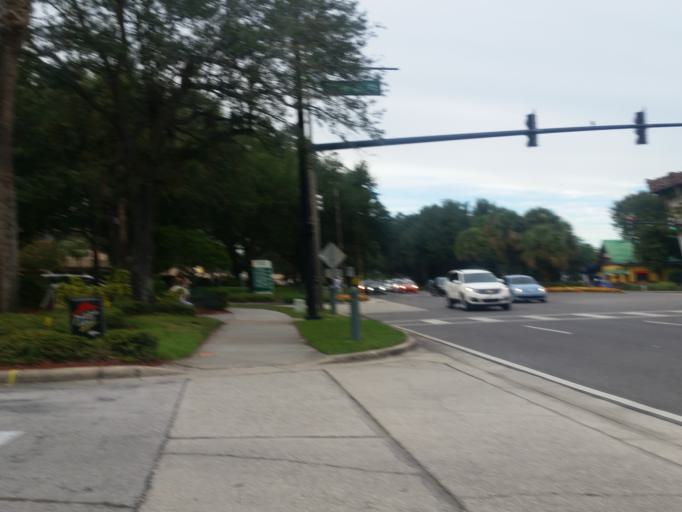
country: US
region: Florida
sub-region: Orange County
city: Doctor Phillips
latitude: 28.4329
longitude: -81.4718
